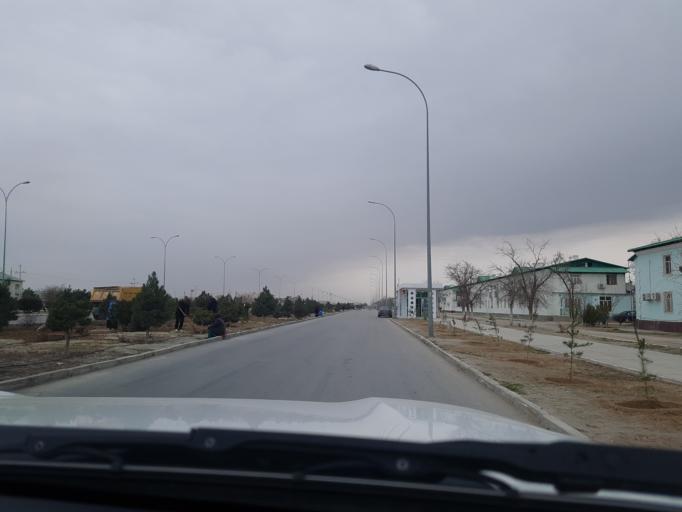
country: TM
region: Balkan
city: Balkanabat
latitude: 39.5089
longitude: 54.3491
